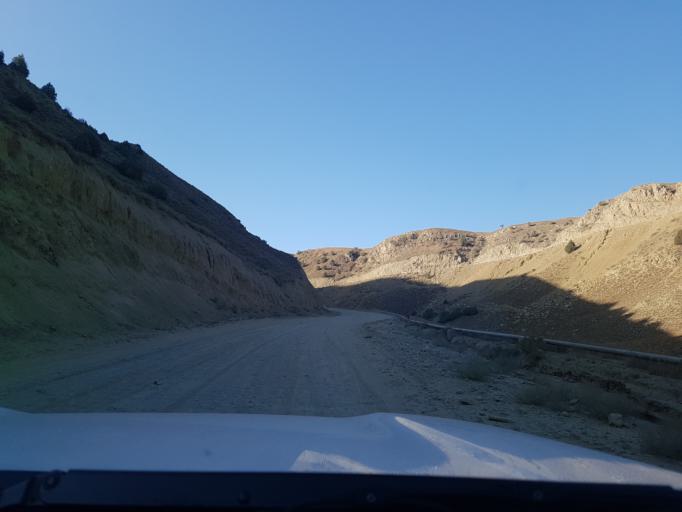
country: TM
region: Ahal
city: Baharly
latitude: 38.4451
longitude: 57.0489
